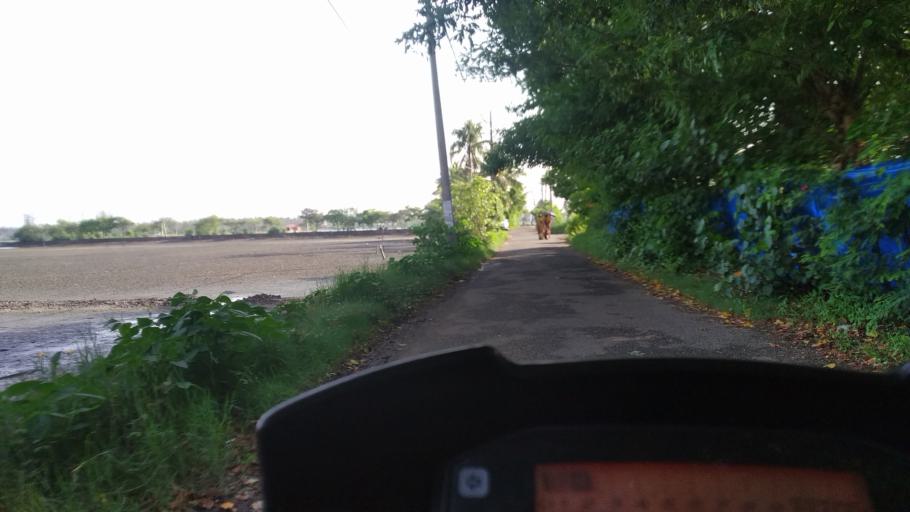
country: IN
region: Kerala
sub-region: Thrissur District
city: Kodungallur
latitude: 10.1322
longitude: 76.1899
